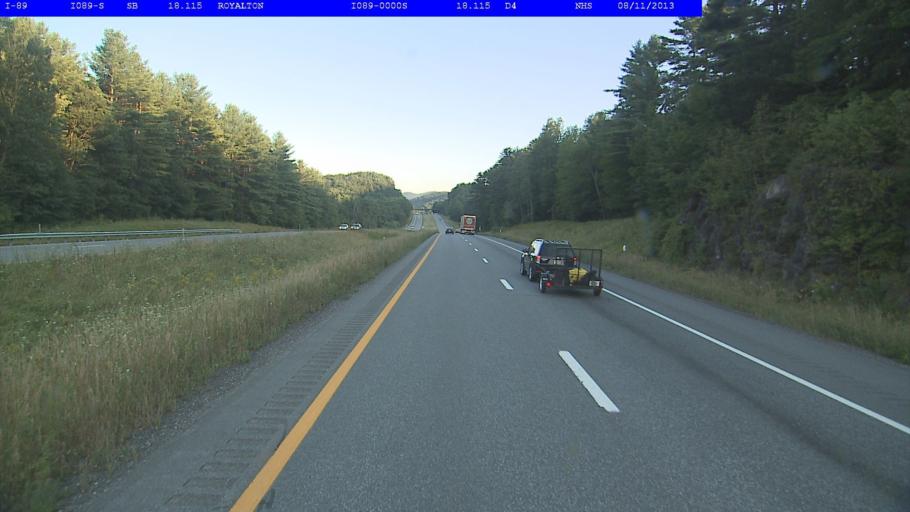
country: US
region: Vermont
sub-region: Orange County
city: Randolph
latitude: 43.8155
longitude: -72.5237
